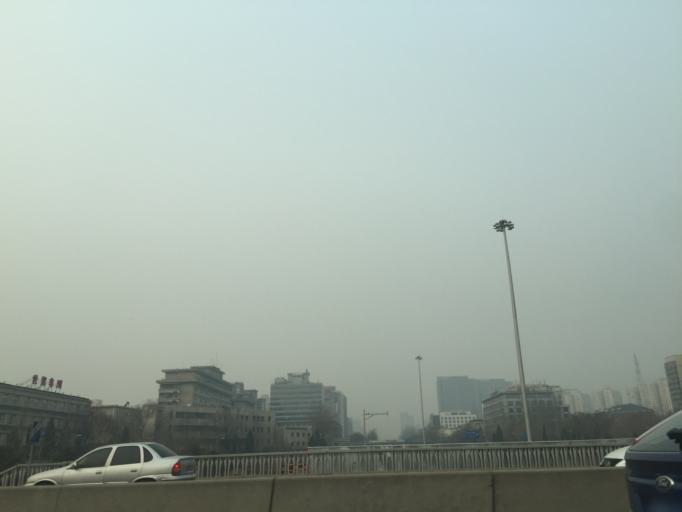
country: CN
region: Beijing
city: Datun
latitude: 39.9669
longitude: 116.3885
